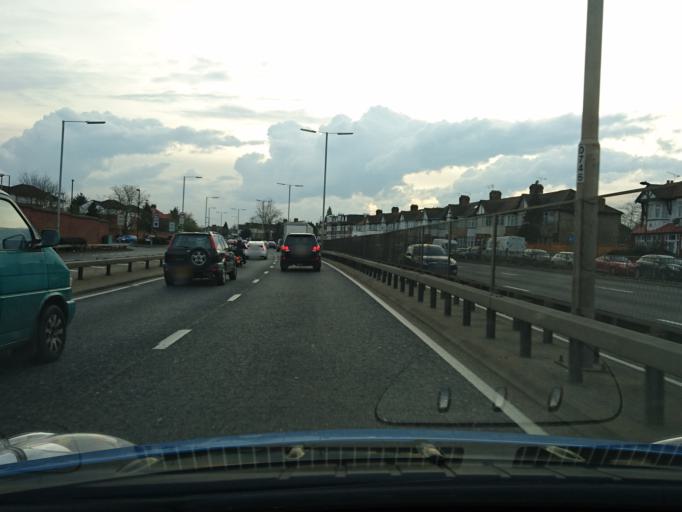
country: GB
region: England
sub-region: Greater London
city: Wood Green
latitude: 51.6161
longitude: -0.0949
